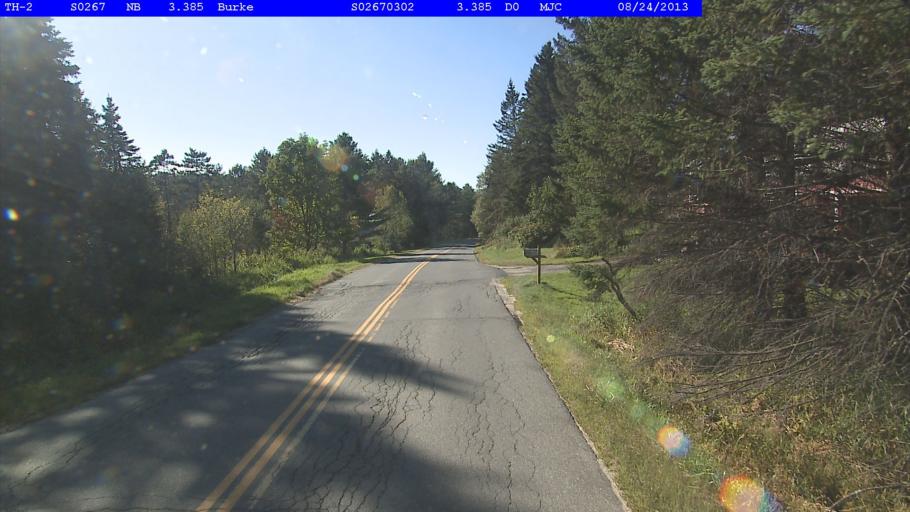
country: US
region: Vermont
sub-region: Caledonia County
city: Lyndonville
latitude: 44.6257
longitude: -71.9603
